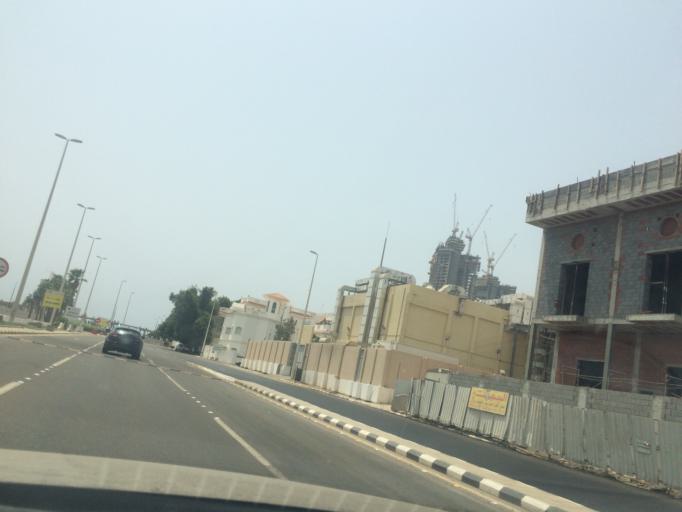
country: SA
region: Makkah
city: Jeddah
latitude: 21.5909
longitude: 39.1132
